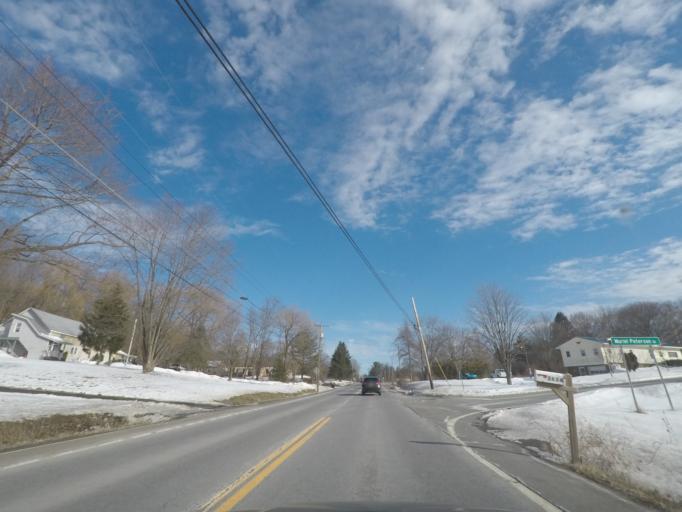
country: US
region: New York
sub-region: Albany County
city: Altamont
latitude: 42.7791
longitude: -74.0573
